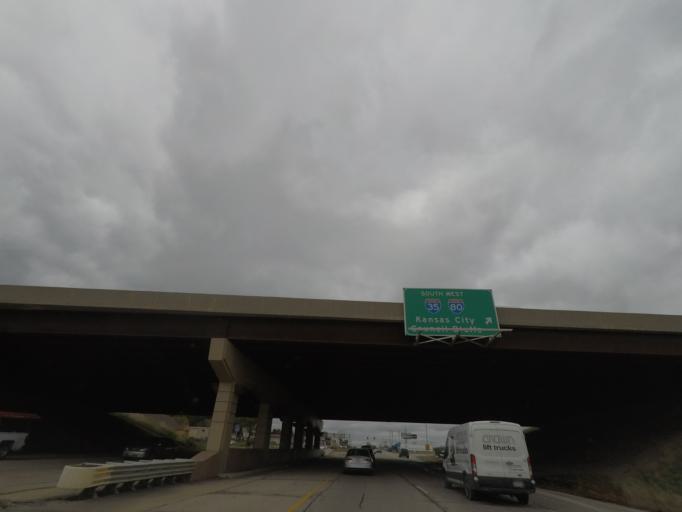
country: US
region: Iowa
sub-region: Polk County
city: Saylorville
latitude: 41.6482
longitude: -93.6006
